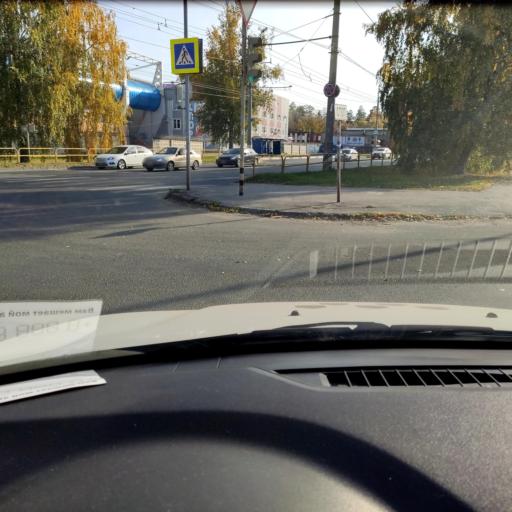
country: RU
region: Samara
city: Tol'yatti
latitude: 53.5012
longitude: 49.3896
